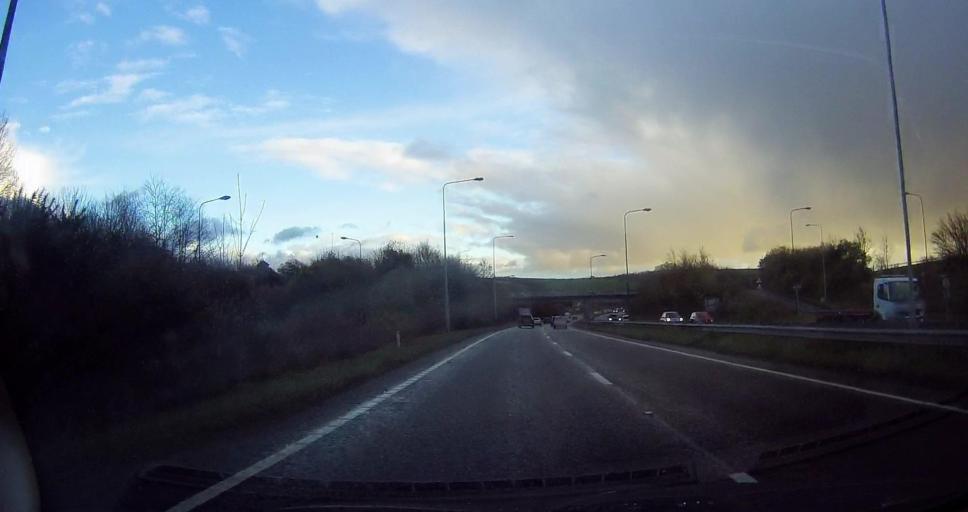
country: GB
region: England
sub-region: West Sussex
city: Hassocks
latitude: 50.8990
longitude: -0.1686
